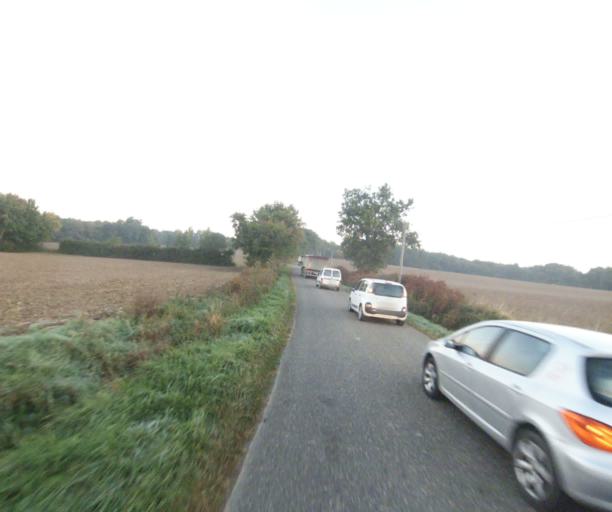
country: FR
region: Midi-Pyrenees
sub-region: Departement du Gers
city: Vic-Fezensac
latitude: 43.7810
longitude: 0.2220
